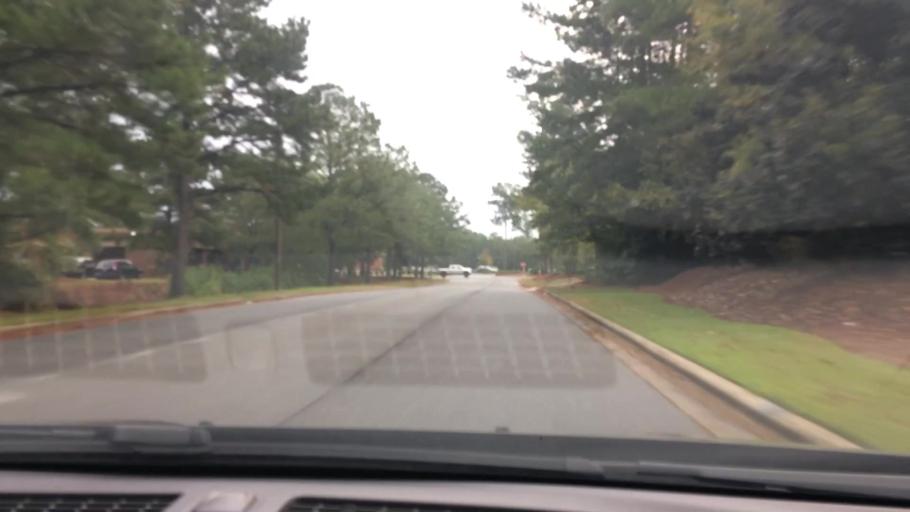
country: US
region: North Carolina
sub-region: Pitt County
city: Windsor
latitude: 35.5713
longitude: -77.3606
